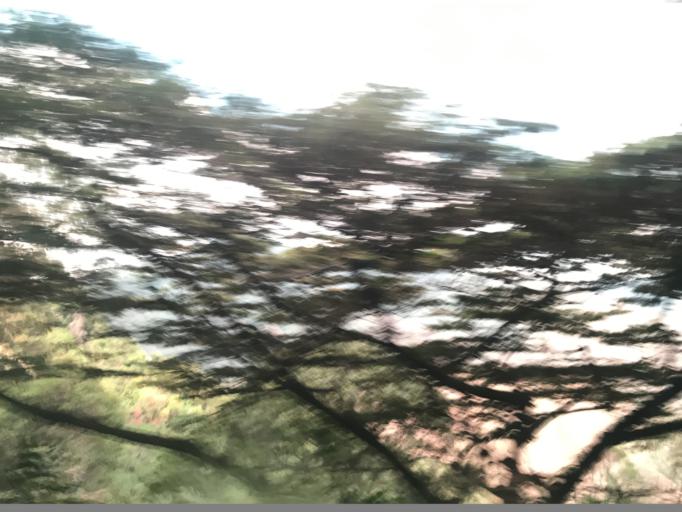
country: CO
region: Valle del Cauca
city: Cali
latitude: 3.4784
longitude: -76.6007
